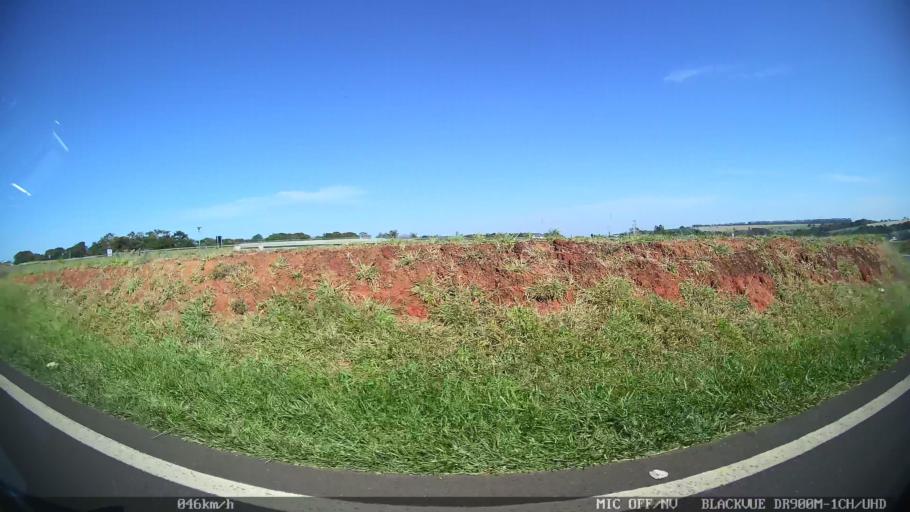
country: BR
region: Sao Paulo
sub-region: Franca
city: Franca
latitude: -20.5604
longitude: -47.4130
